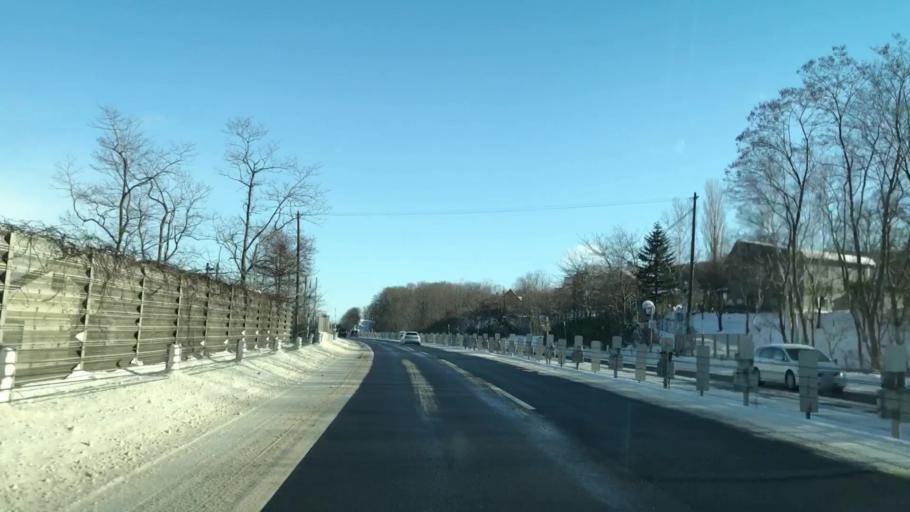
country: JP
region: Hokkaido
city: Sapporo
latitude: 43.1196
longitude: 141.2221
